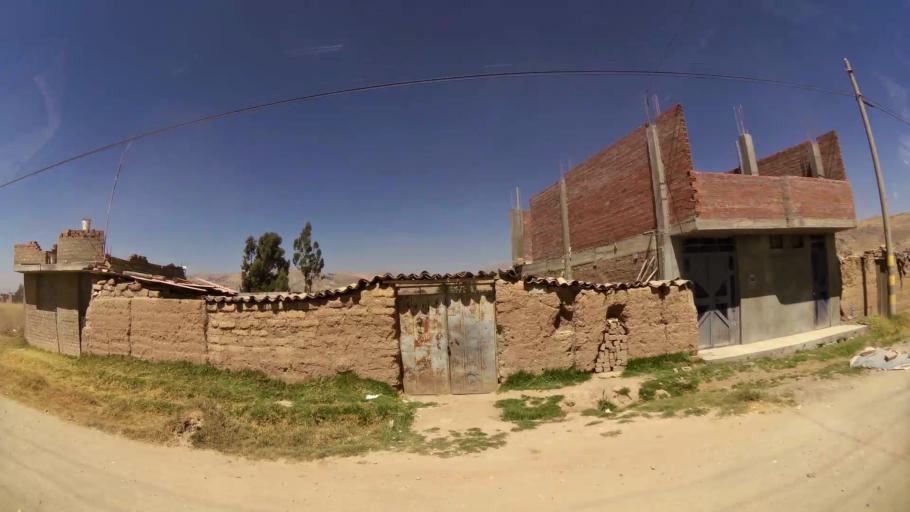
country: PE
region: Junin
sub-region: Provincia de Jauja
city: Jauja
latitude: -11.7791
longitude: -75.4881
